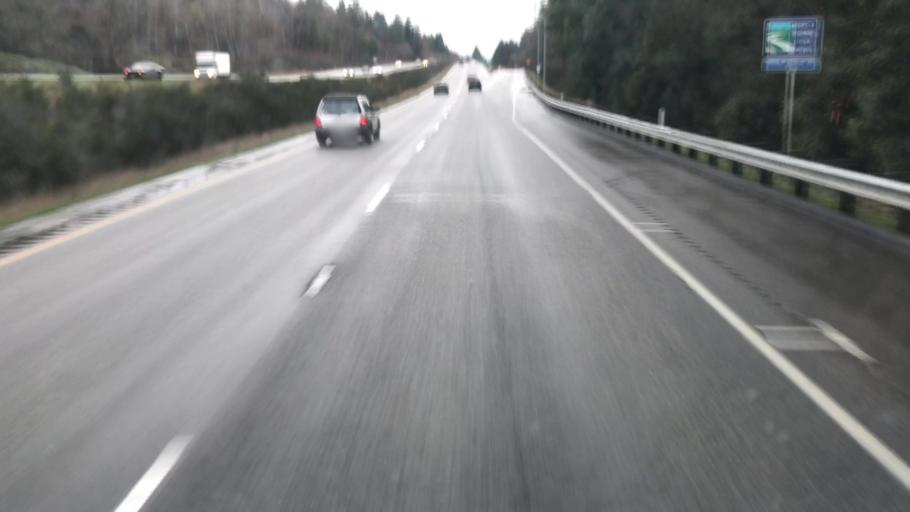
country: US
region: Washington
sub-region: Kitsap County
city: Burley
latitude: 47.4371
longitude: -122.6231
